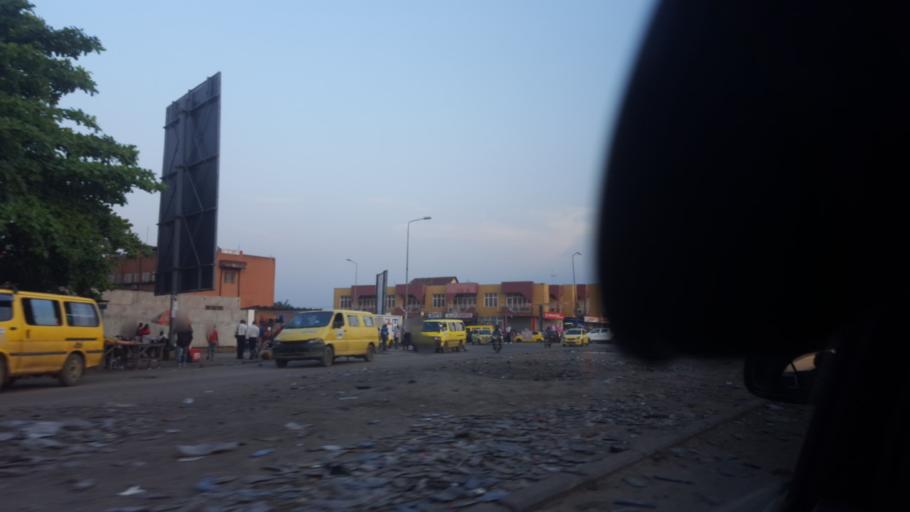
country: CD
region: Kinshasa
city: Kinshasa
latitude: -4.3503
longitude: 15.3249
